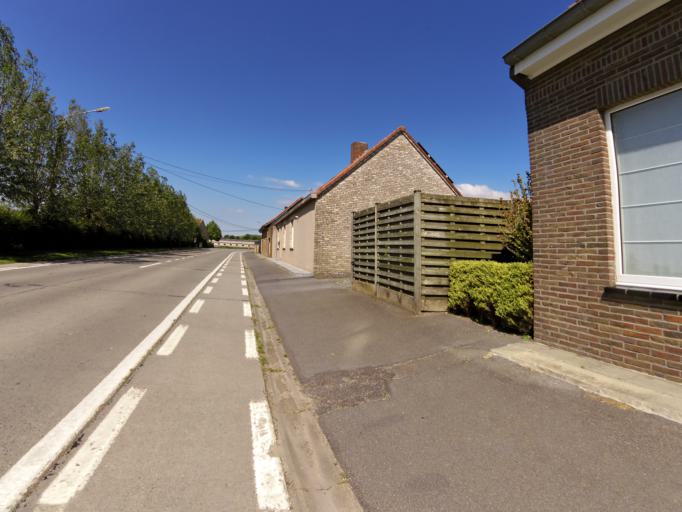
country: BE
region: Flanders
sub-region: Provincie West-Vlaanderen
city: Koekelare
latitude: 51.0528
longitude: 2.9346
